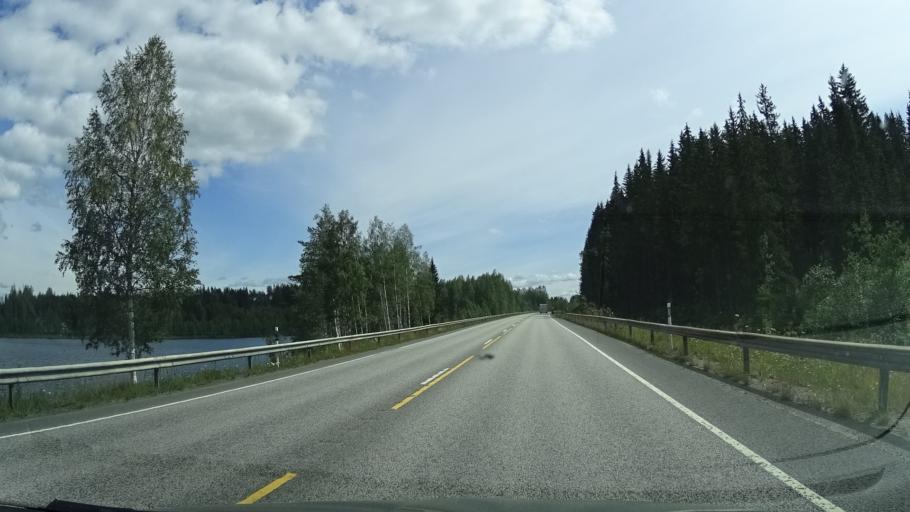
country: FI
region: Central Finland
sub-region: Jyvaeskylae
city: Jyvaeskylae
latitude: 62.2568
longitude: 25.6167
